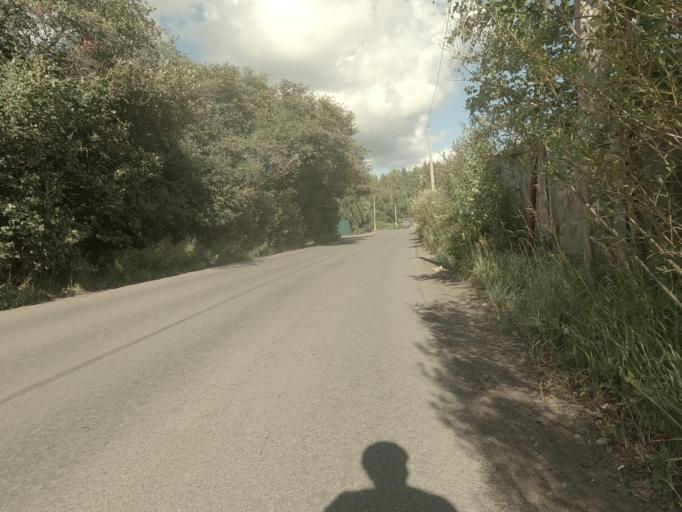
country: RU
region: Leningrad
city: Vsevolozhsk
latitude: 60.0053
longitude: 30.6445
